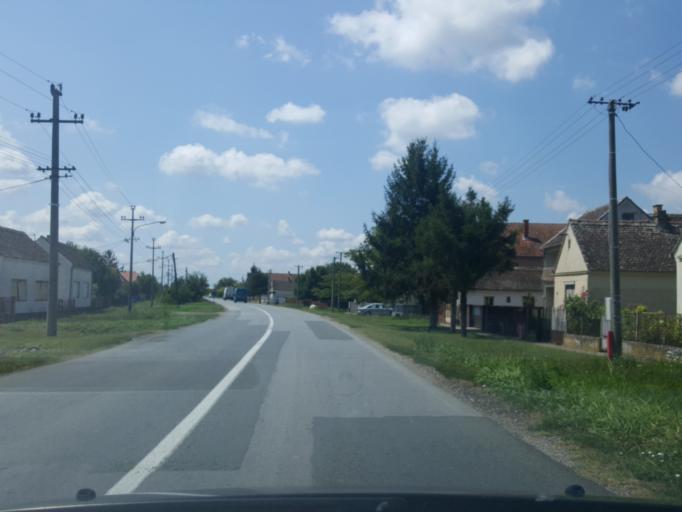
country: RS
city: Salas Nocajski
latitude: 44.9439
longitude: 19.5795
